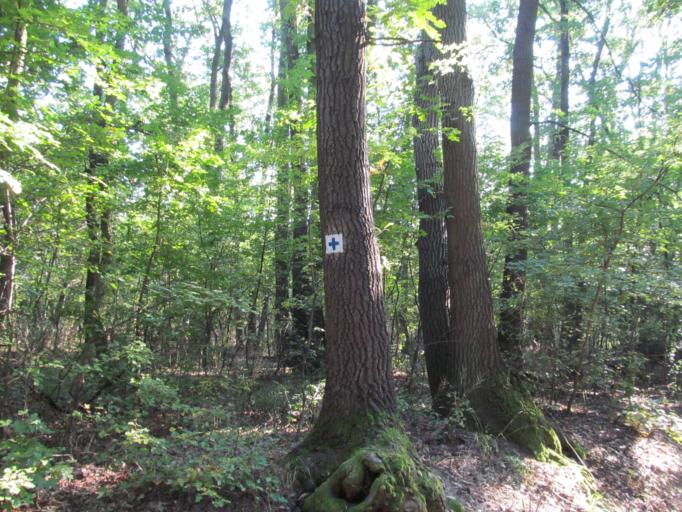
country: HU
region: Pest
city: Szob
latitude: 47.8962
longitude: 18.8085
